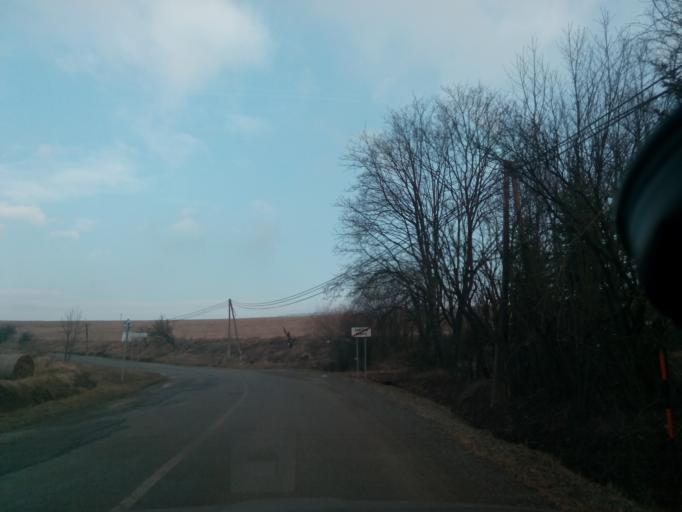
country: SK
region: Presovsky
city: Lipany
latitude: 49.1773
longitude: 20.8551
